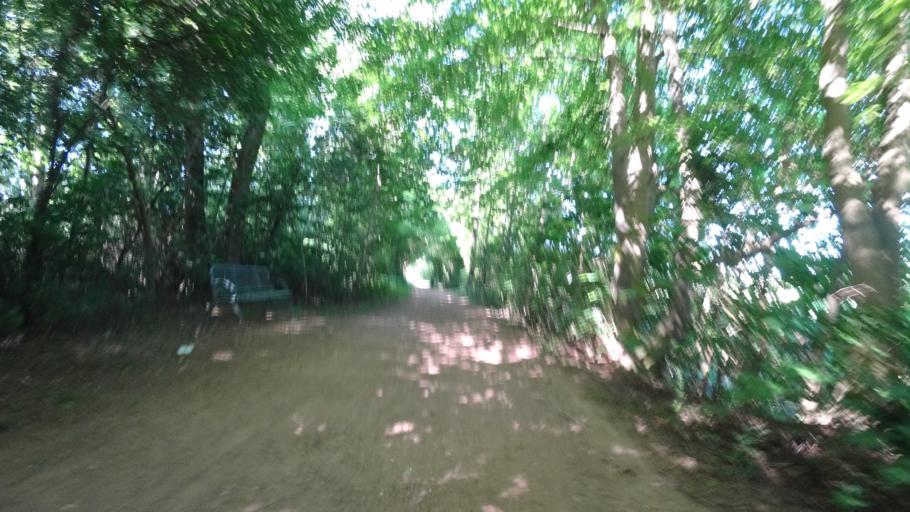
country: DE
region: North Rhine-Westphalia
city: Erwitte
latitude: 51.6376
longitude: 8.3610
